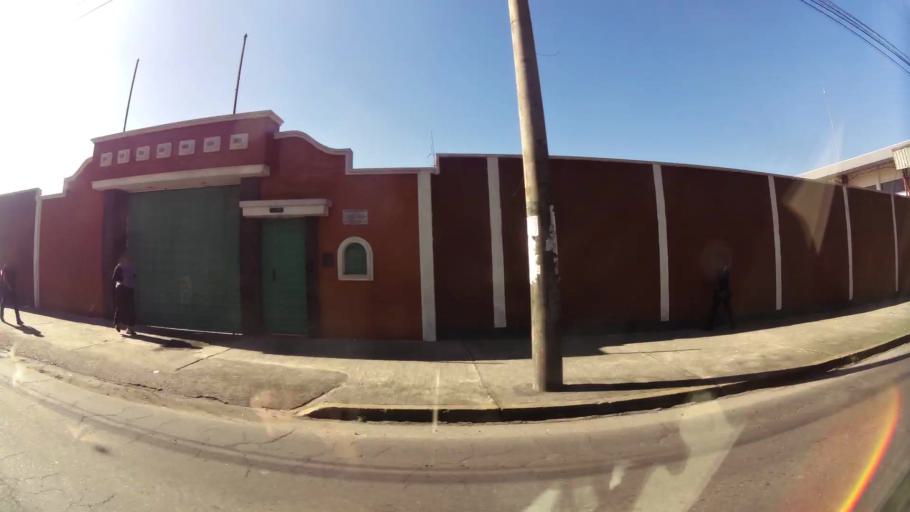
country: EC
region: Pichincha
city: Quito
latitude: -0.2373
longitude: -78.5282
